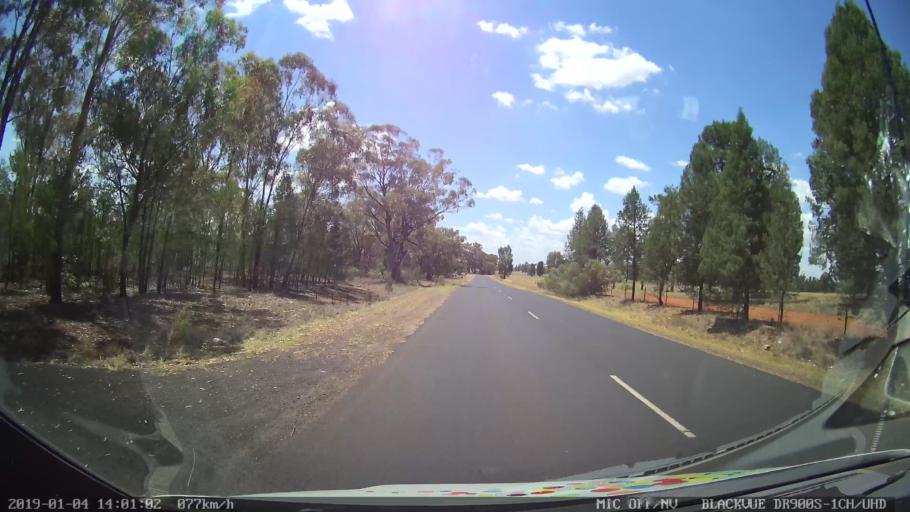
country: AU
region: New South Wales
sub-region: Dubbo Municipality
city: Dubbo
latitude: -32.3011
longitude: 148.5974
